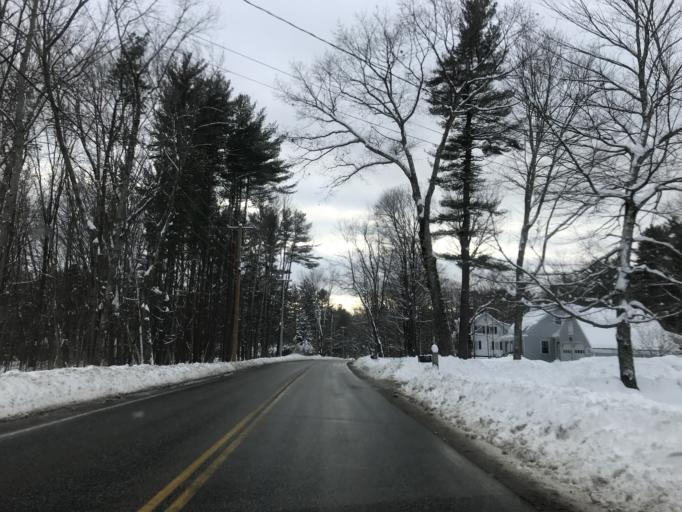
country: US
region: Maine
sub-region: Cumberland County
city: Falmouth
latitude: 43.7275
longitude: -70.3118
